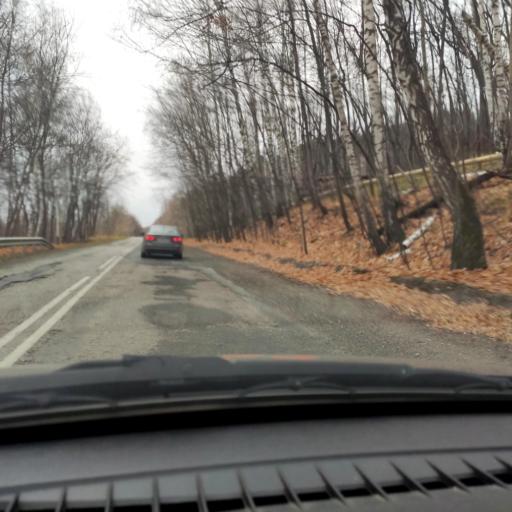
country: RU
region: Samara
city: Pribrezhnyy
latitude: 53.4383
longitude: 49.7262
